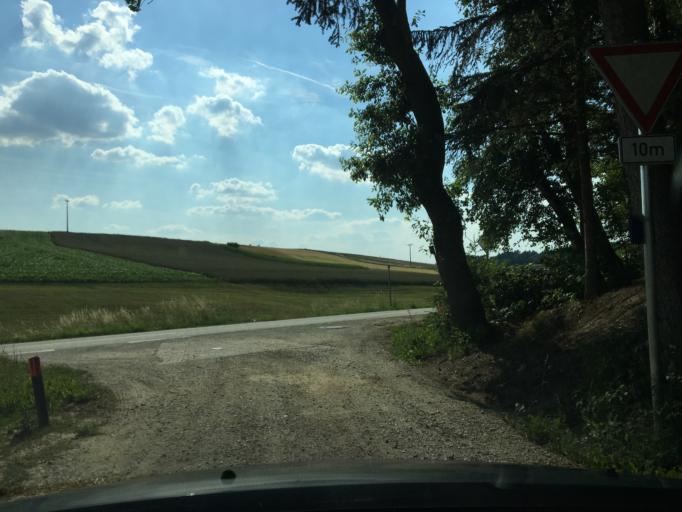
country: DE
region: Bavaria
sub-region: Upper Bavaria
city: Kirchberg
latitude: 48.4470
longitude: 12.0499
